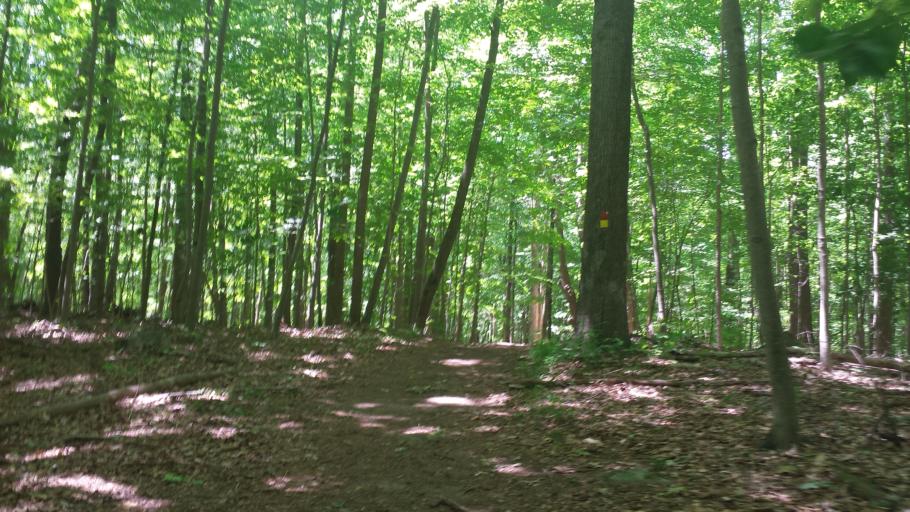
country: US
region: New York
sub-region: Westchester County
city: Pound Ridge
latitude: 41.2452
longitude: -73.5847
